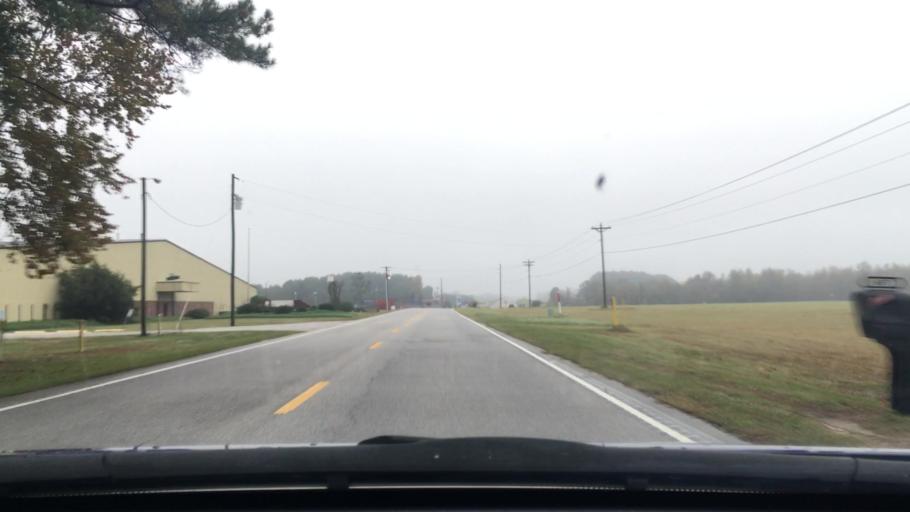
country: US
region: South Carolina
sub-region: Florence County
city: Timmonsville
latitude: 34.2109
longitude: -80.0201
